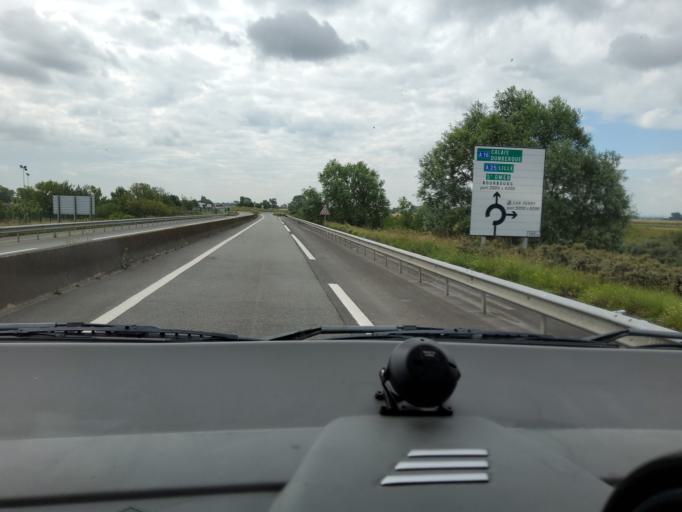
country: FR
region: Nord-Pas-de-Calais
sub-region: Departement du Nord
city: Loon-Plage
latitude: 50.9936
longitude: 2.2019
